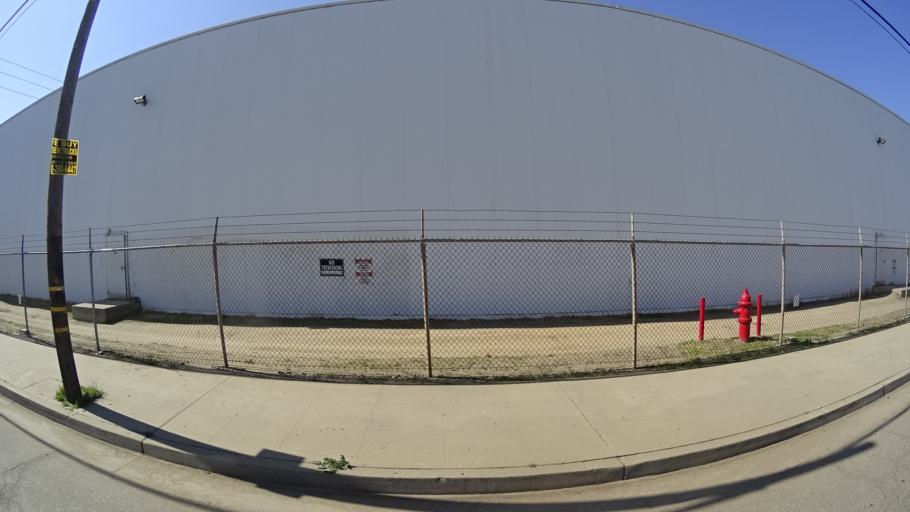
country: US
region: California
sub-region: Fresno County
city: Fresno
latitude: 36.7183
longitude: -119.7548
